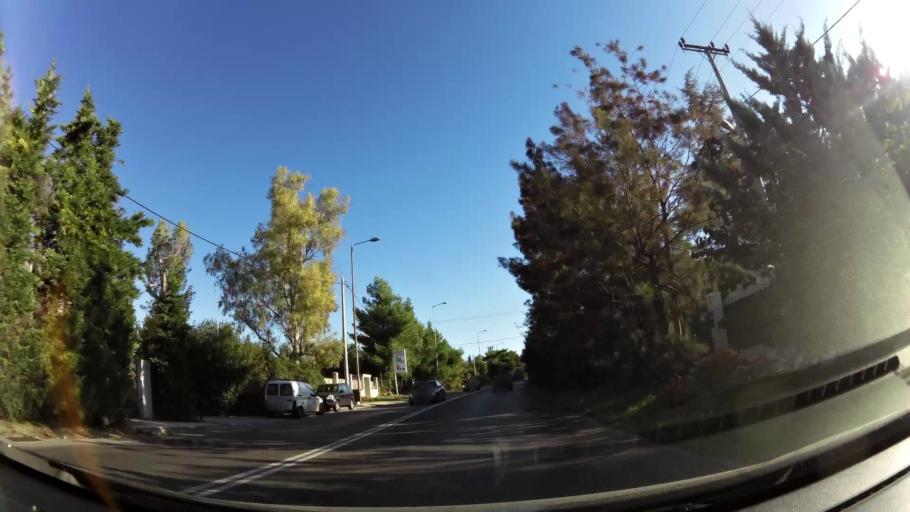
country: GR
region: Attica
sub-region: Nomarchia Athinas
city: Ekali
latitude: 38.1026
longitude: 23.8291
